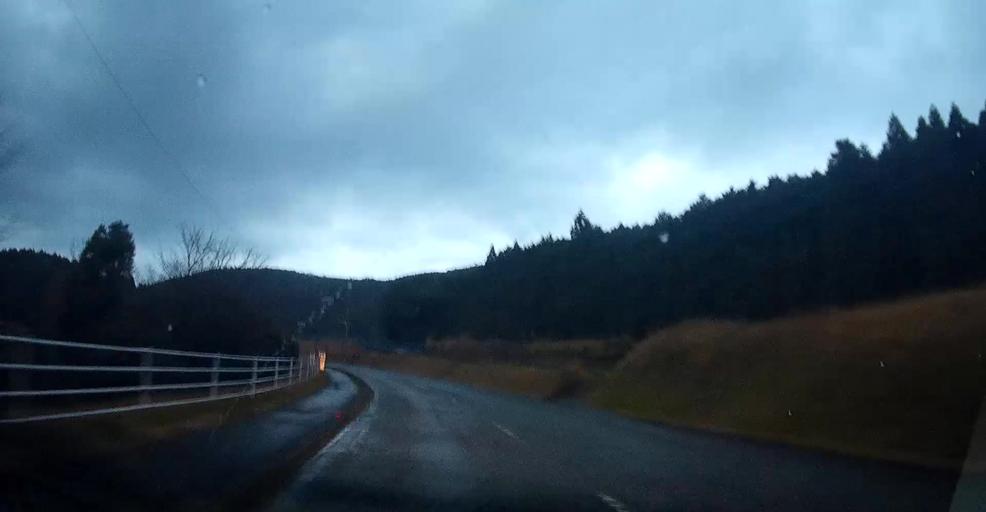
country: JP
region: Kumamoto
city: Ozu
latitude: 32.8306
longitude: 130.9172
